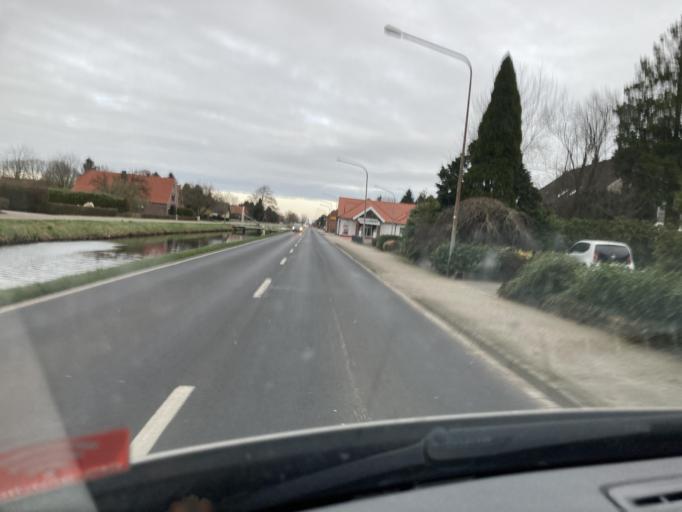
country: DE
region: Lower Saxony
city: Ostrhauderfehn
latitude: 53.1314
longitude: 7.5281
